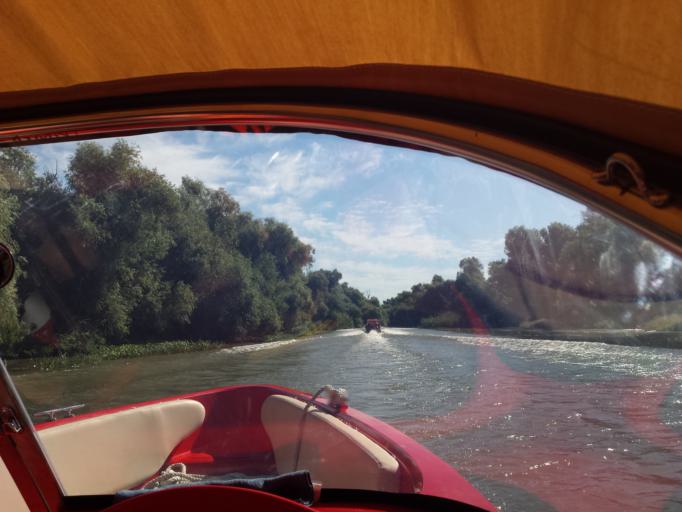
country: RO
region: Tulcea
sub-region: Comuna Pardina
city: Pardina
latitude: 45.2501
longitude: 29.0440
